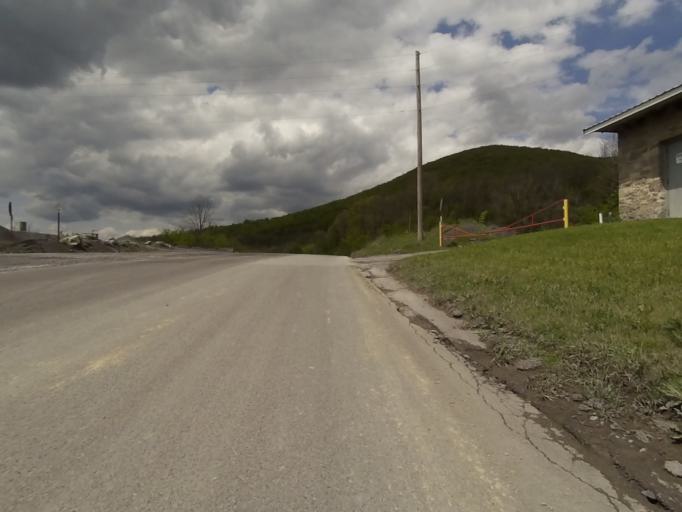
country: US
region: Pennsylvania
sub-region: Centre County
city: Lemont
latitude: 40.7983
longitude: -77.8049
